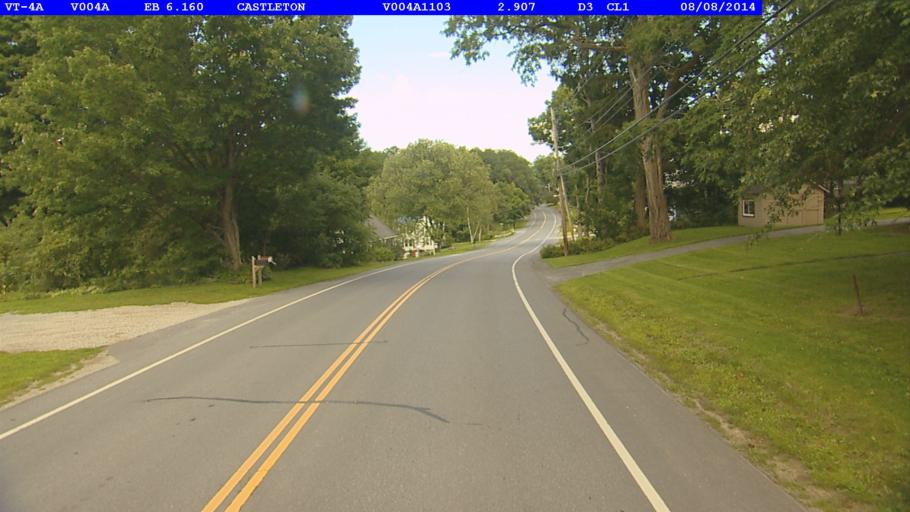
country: US
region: Vermont
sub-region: Rutland County
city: Castleton
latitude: 43.6097
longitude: -73.1868
